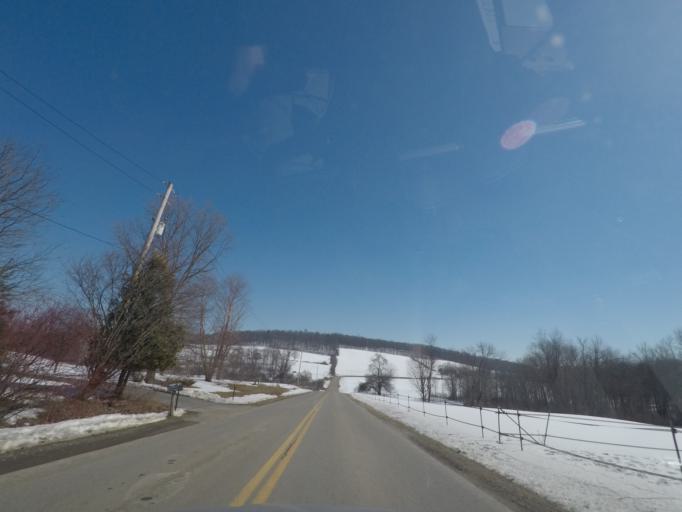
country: US
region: New York
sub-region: Saratoga County
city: Stillwater
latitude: 43.0319
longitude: -73.6779
